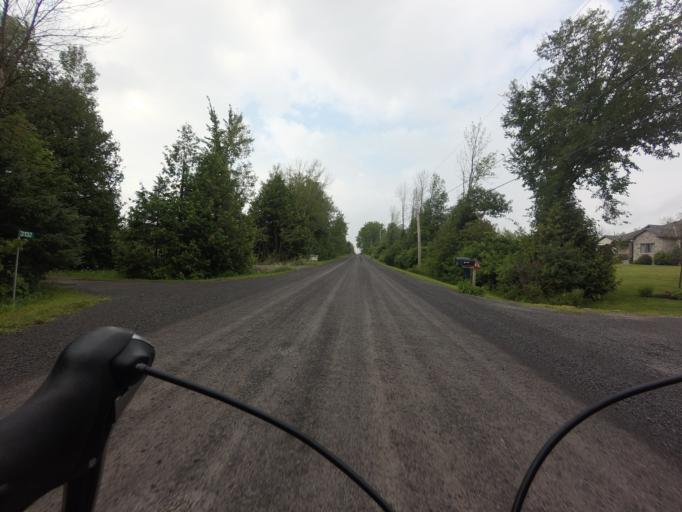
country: CA
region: Ontario
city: Bells Corners
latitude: 45.1097
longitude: -75.7908
